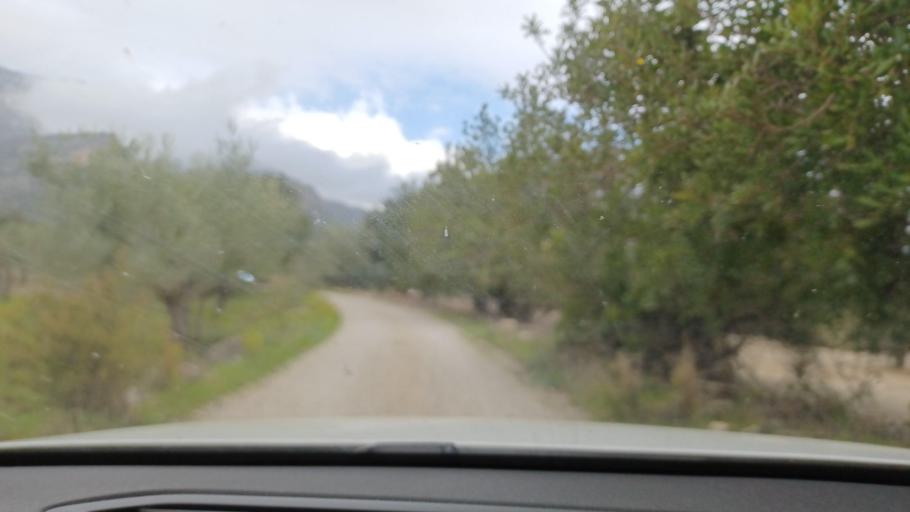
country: ES
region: Catalonia
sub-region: Provincia de Tarragona
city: Mas de Barberans
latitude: 40.8032
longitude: 0.4135
